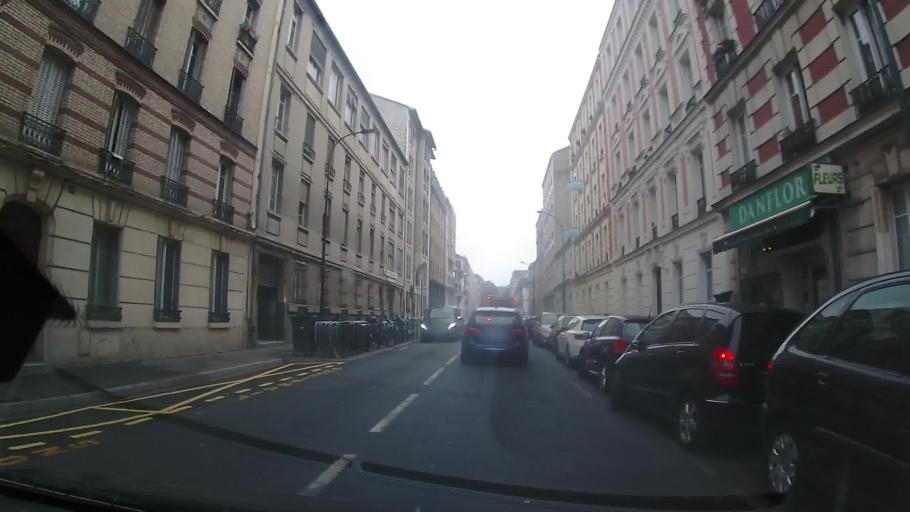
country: FR
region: Ile-de-France
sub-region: Departement des Hauts-de-Seine
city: Clichy
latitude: 48.9014
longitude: 2.3092
